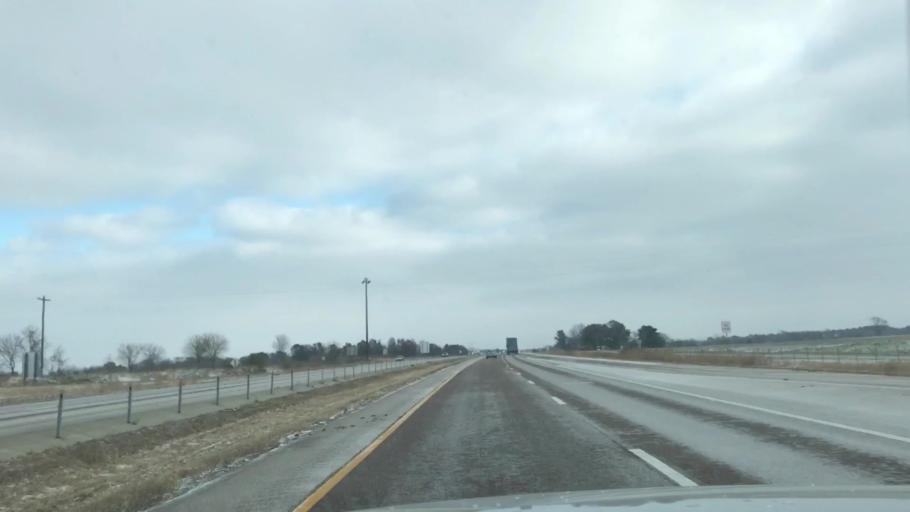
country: US
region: Illinois
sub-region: Madison County
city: Worden
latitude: 38.9330
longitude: -89.7998
